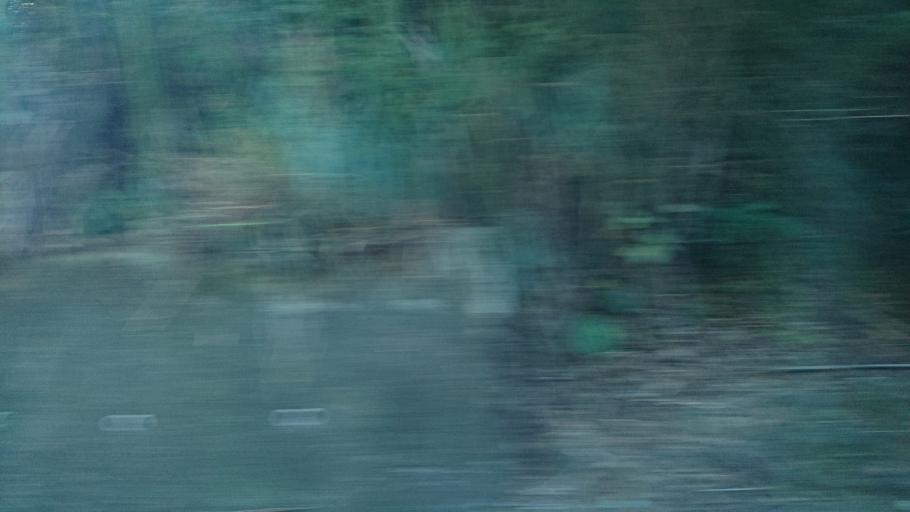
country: TW
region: Taiwan
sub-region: Yunlin
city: Douliu
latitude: 23.5324
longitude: 120.6611
